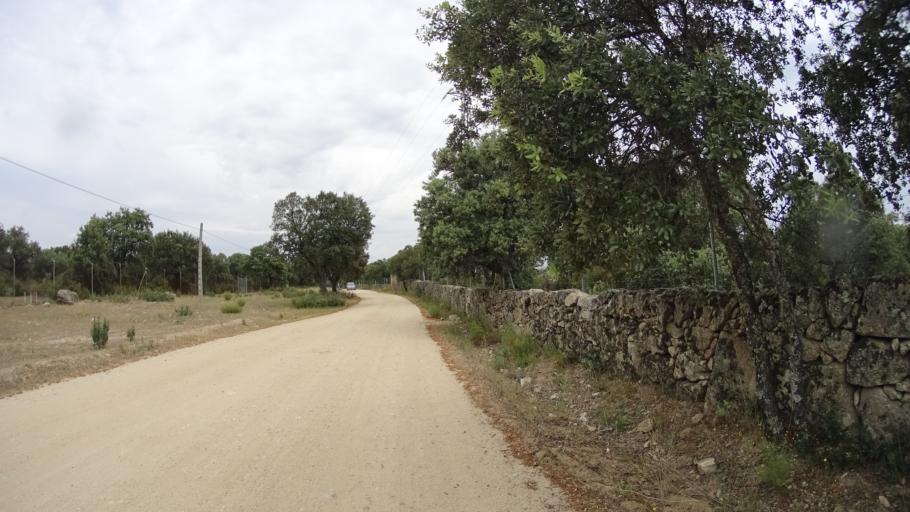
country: ES
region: Madrid
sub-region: Provincia de Madrid
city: Colmenarejo
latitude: 40.5518
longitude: -4.0379
